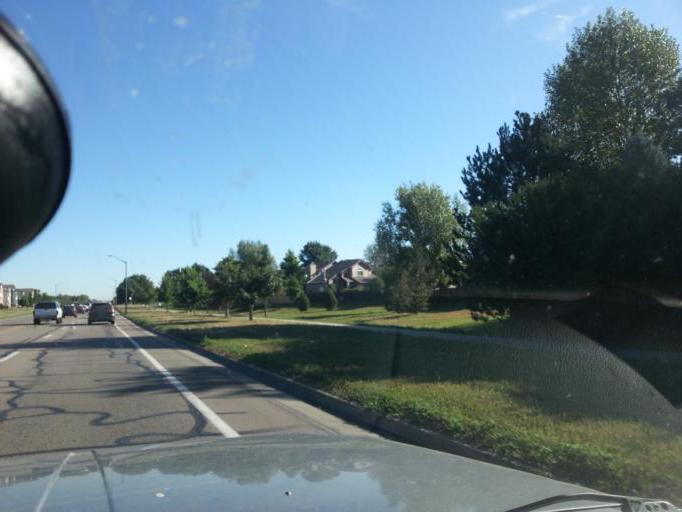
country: US
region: Colorado
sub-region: Larimer County
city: Fort Collins
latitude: 40.5264
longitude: -105.0393
